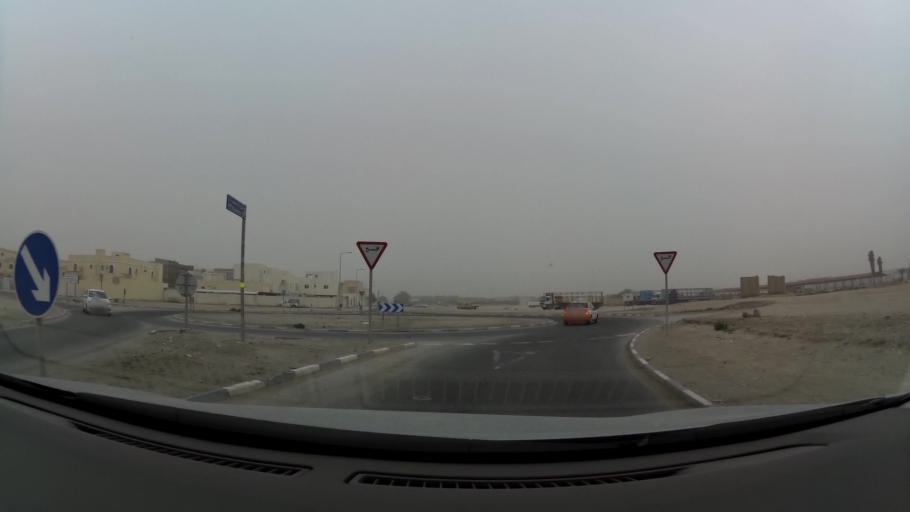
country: QA
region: Baladiyat ad Dawhah
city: Doha
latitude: 25.2396
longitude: 51.4850
